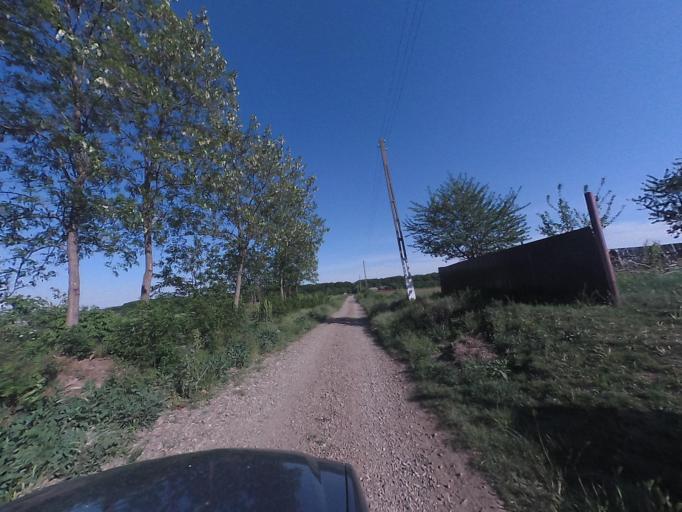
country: RO
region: Neamt
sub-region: Comuna Dulcesti
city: Dulcesti
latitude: 46.9994
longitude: 26.7794
